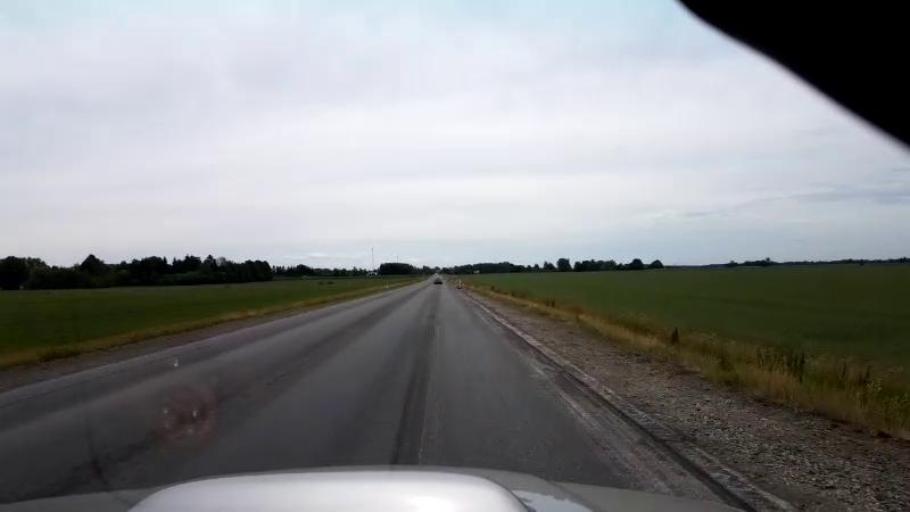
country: LV
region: Bauskas Rajons
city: Bauska
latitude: 56.3731
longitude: 24.2694
